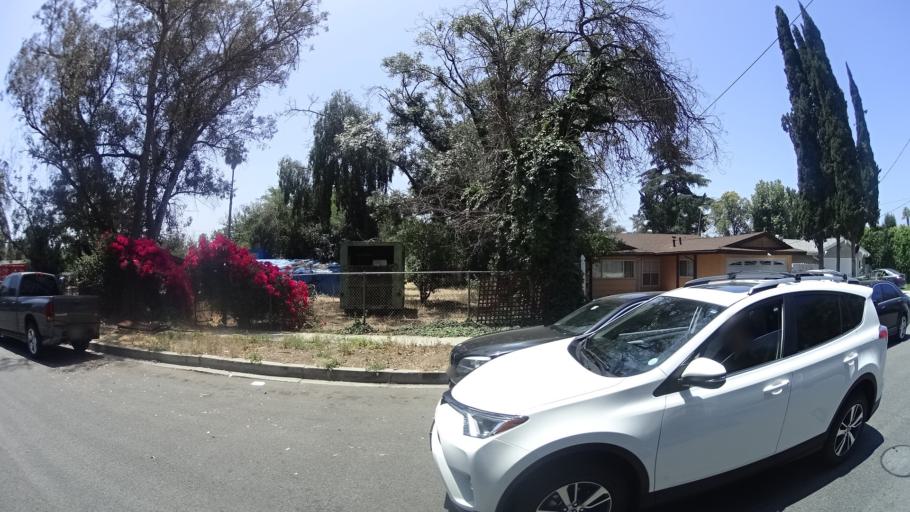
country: US
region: California
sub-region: Los Angeles County
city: Van Nuys
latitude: 34.2058
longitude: -118.4426
